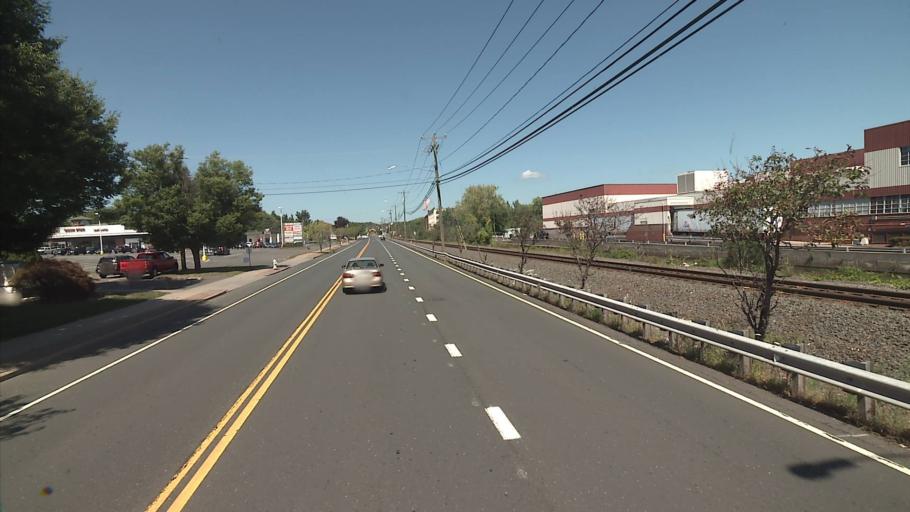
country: US
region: Connecticut
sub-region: Hartford County
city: Windsor Locks
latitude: 41.9265
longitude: -72.6273
